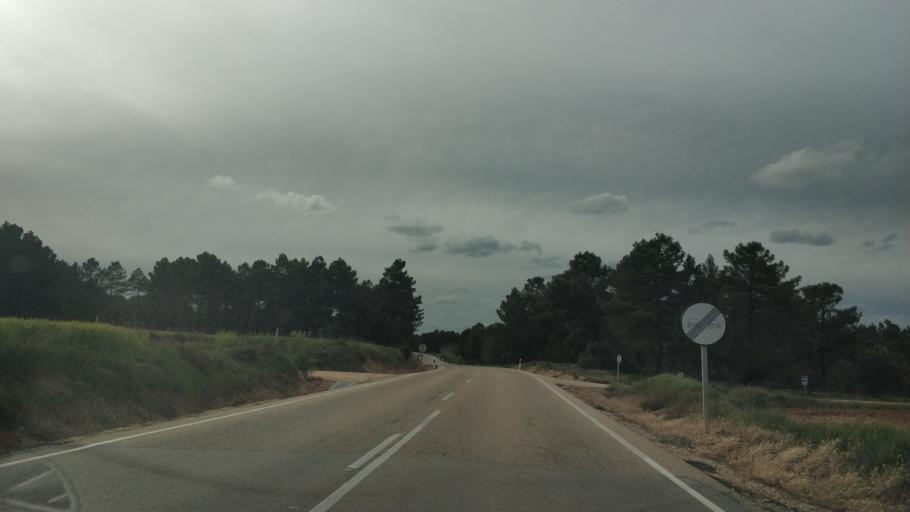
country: ES
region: Castille and Leon
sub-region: Provincia de Soria
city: Valdenebro
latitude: 41.5556
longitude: -2.9654
